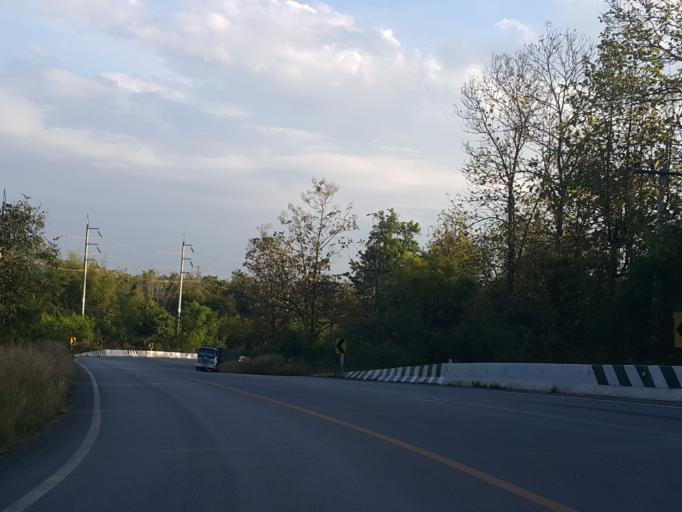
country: TH
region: Lampang
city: Lampang
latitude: 18.4338
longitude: 99.5422
